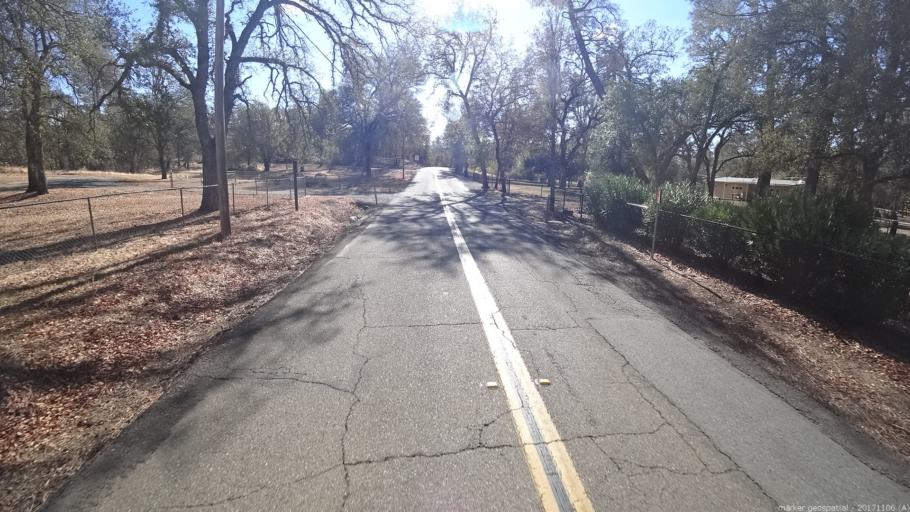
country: US
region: California
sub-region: Shasta County
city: Bella Vista
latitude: 40.6170
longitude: -122.2780
